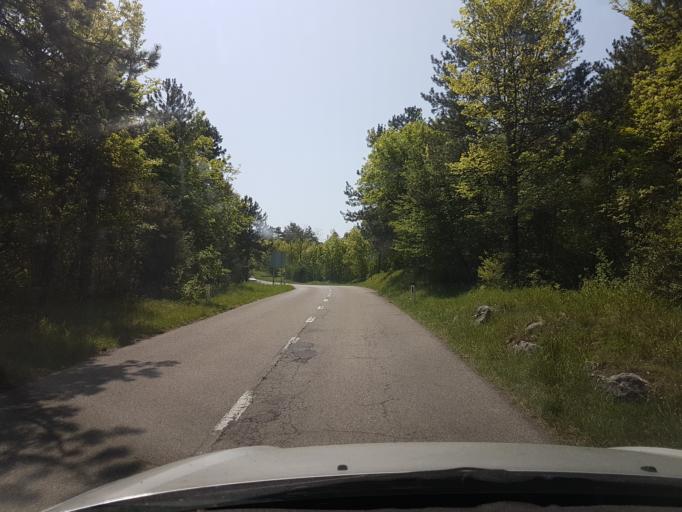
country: IT
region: Friuli Venezia Giulia
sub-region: Provincia di Trieste
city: Aurisina
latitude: 45.7824
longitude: 13.6997
